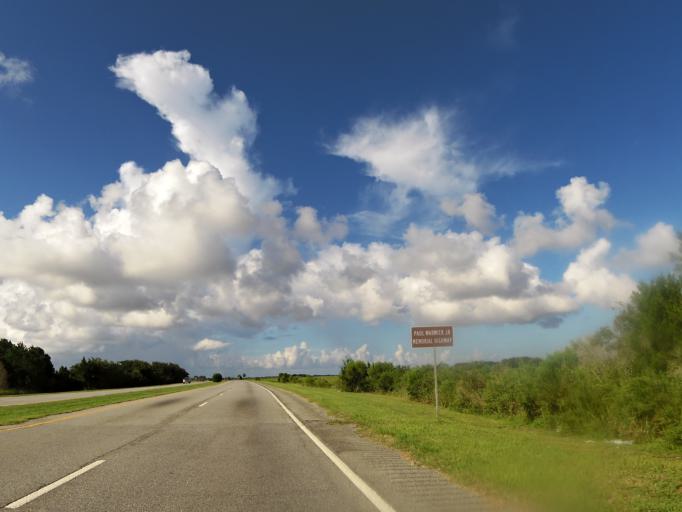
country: US
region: Georgia
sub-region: Glynn County
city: Brunswick
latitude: 31.1296
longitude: -81.4795
